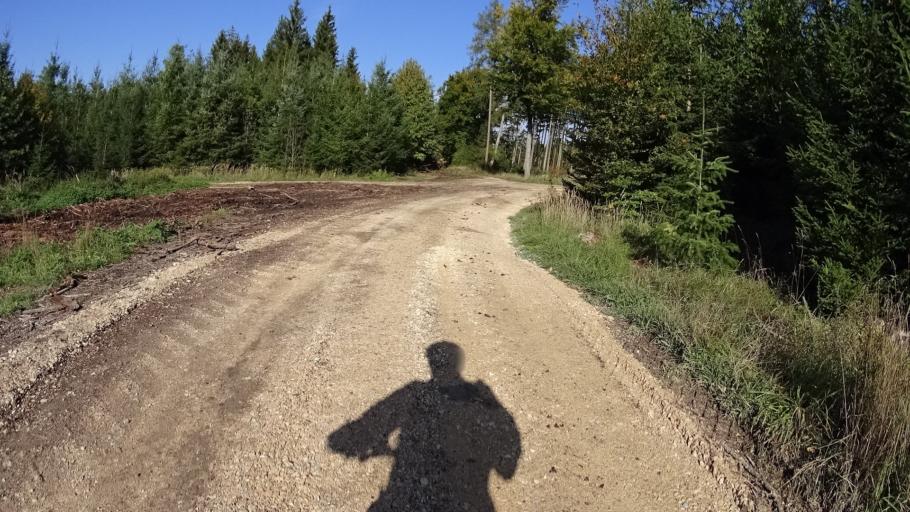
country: DE
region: Bavaria
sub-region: Upper Bavaria
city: Bohmfeld
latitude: 48.8800
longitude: 11.3654
